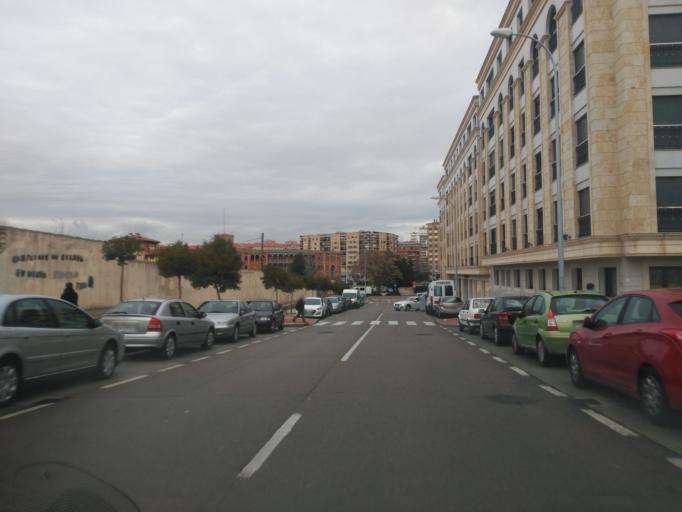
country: ES
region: Castille and Leon
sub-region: Provincia de Salamanca
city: Salamanca
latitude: 40.9773
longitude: -5.6644
